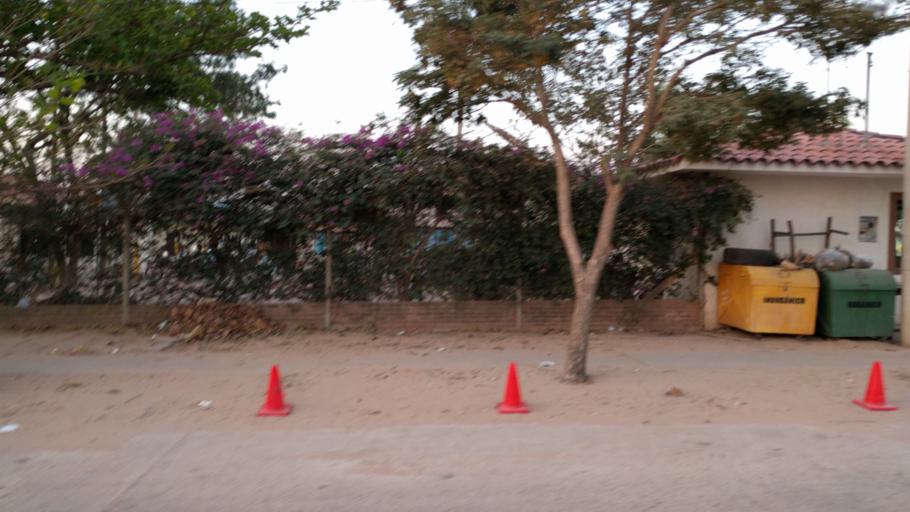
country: BO
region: Santa Cruz
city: Santa Cruz de la Sierra
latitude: -17.7593
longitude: -63.1478
